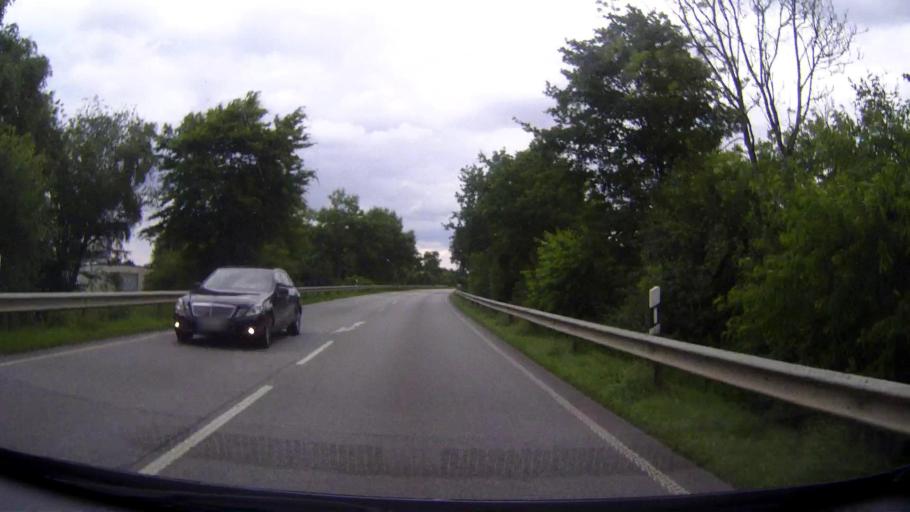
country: DE
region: Schleswig-Holstein
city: Hohenwestedt
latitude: 54.0802
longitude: 9.6537
